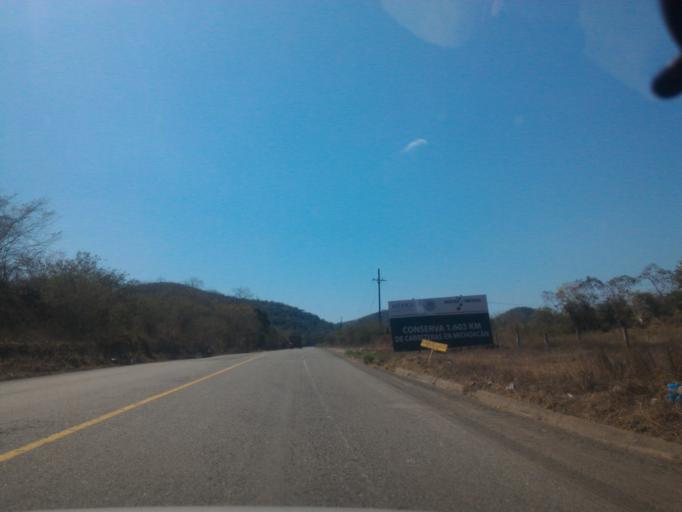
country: MX
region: Michoacan
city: Coahuayana Viejo
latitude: 18.6332
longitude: -103.6678
